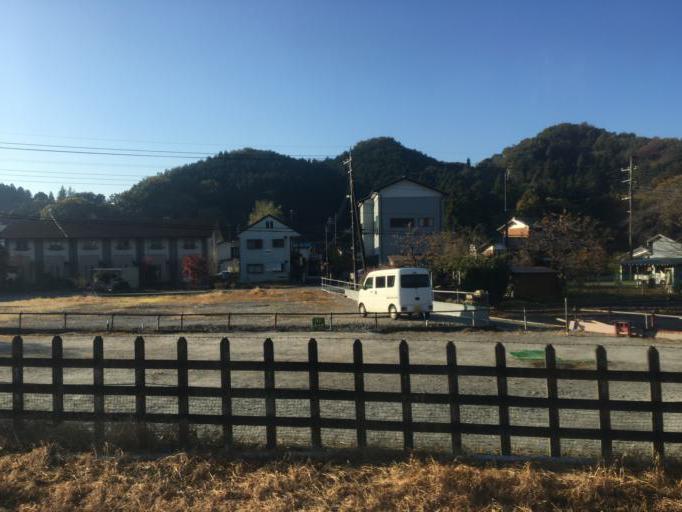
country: JP
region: Saitama
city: Ogawa
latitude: 36.0758
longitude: 139.2292
